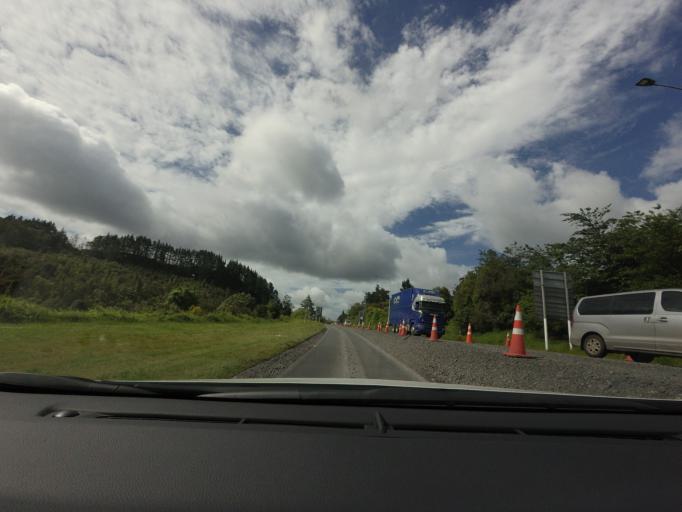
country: NZ
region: Bay of Plenty
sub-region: Rotorua District
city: Rotorua
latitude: -38.1678
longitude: 176.2456
